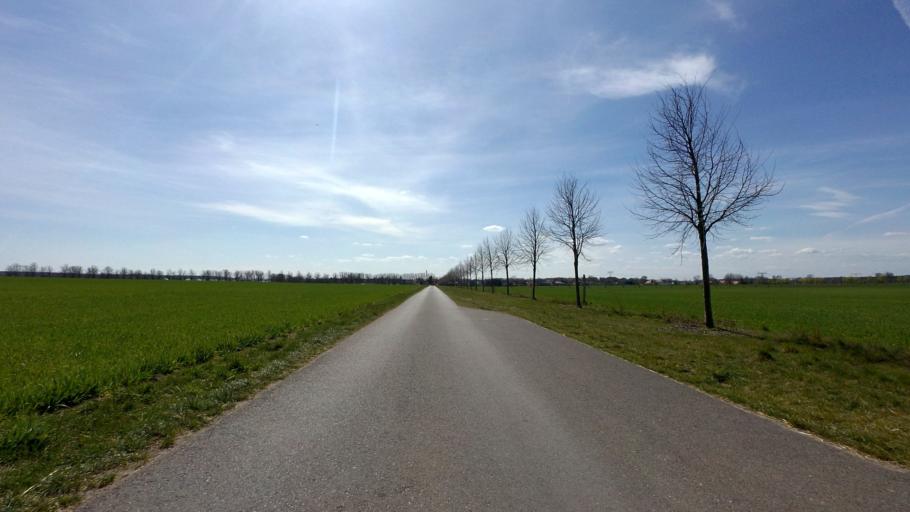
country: DE
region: Brandenburg
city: Schonefeld
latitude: 52.3498
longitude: 13.5227
